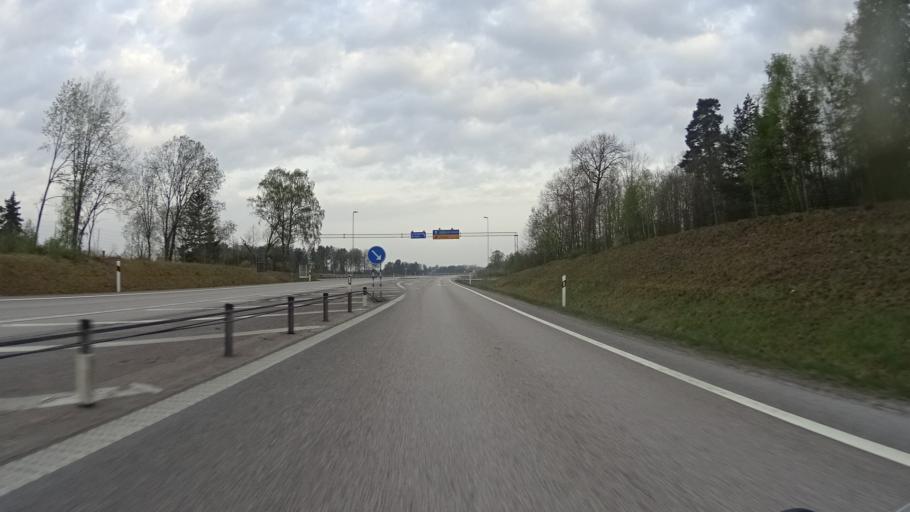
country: SE
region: Vaestra Goetaland
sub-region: Vara Kommun
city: Kvanum
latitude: 58.3443
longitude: 13.2166
